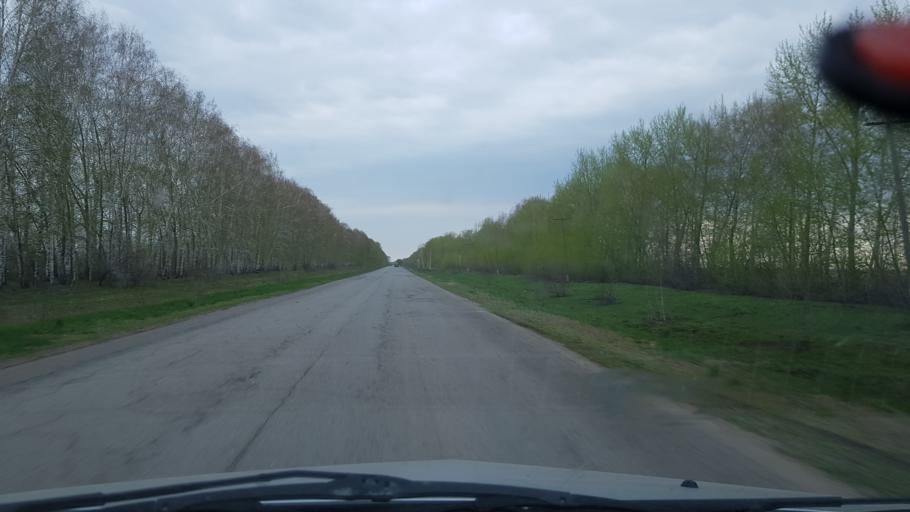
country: RU
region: Samara
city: Podstepki
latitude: 53.6631
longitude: 49.1931
